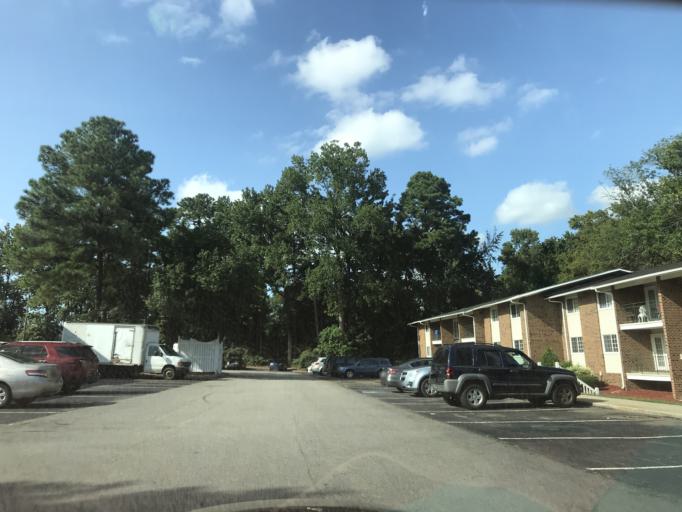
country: US
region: North Carolina
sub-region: Wake County
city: Raleigh
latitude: 35.8383
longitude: -78.5983
